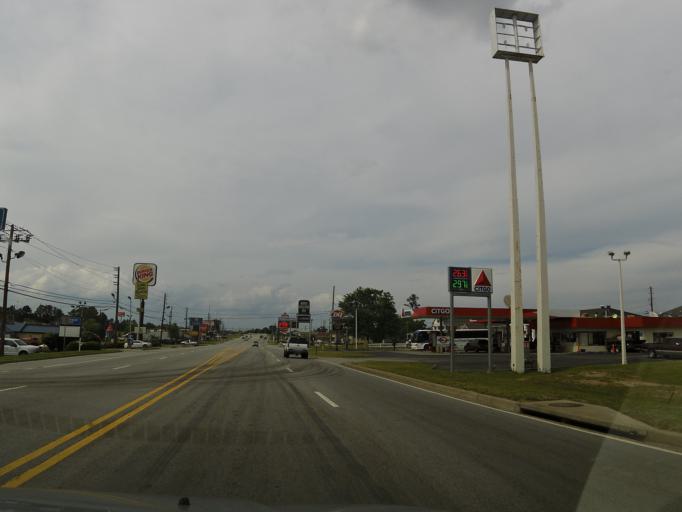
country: US
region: Georgia
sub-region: McDuffie County
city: Thomson
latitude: 33.5061
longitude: -82.5029
